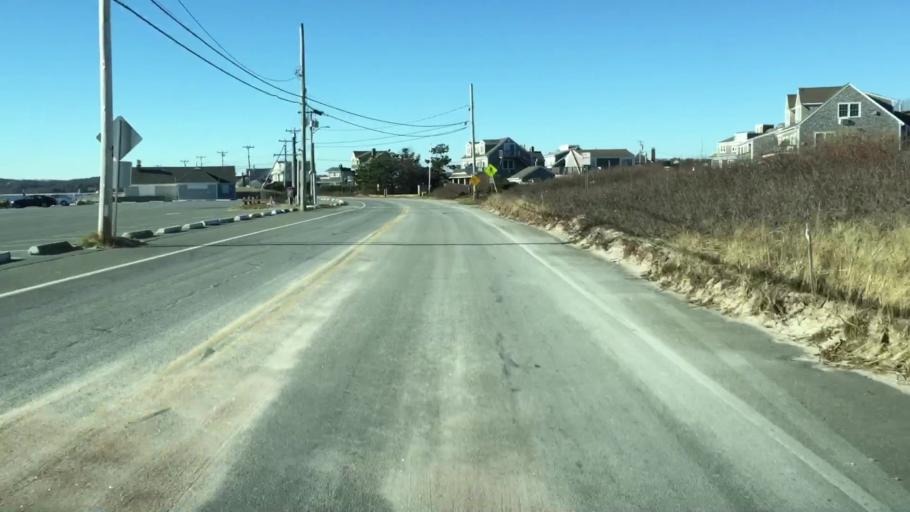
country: US
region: Massachusetts
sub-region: Barnstable County
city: Falmouth
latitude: 41.5427
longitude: -70.6165
